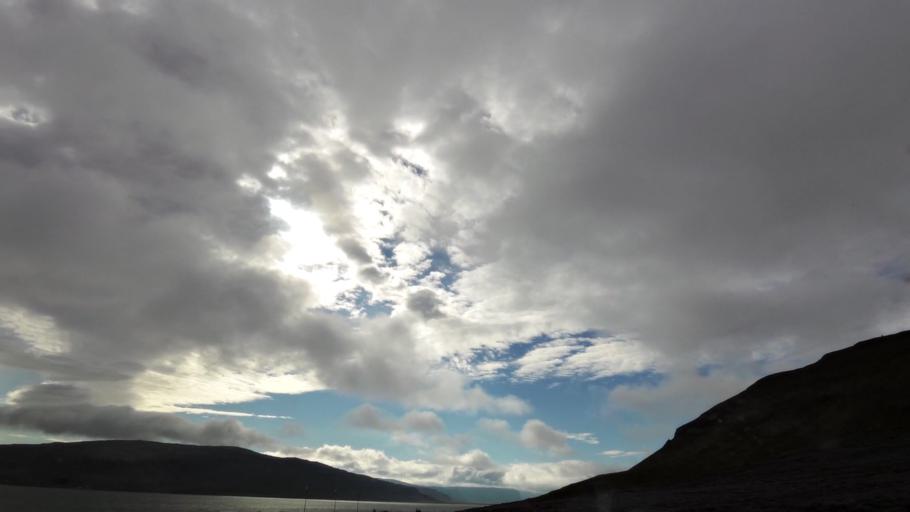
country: IS
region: West
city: Olafsvik
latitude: 65.5431
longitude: -23.8746
